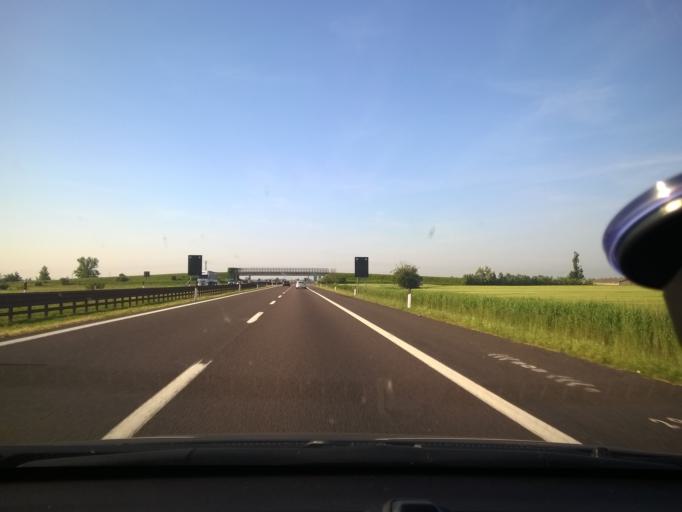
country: IT
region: Emilia-Romagna
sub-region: Provincia di Reggio Emilia
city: Rolo
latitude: 44.8576
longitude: 10.8515
